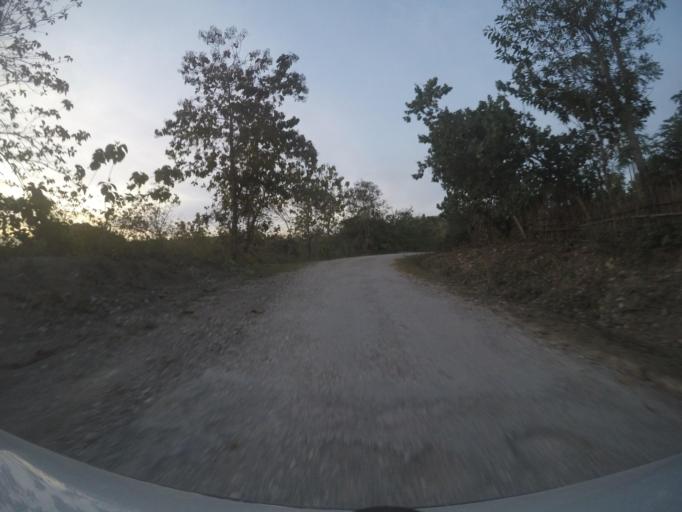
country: TL
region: Viqueque
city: Viqueque
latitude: -8.8872
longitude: 126.3861
